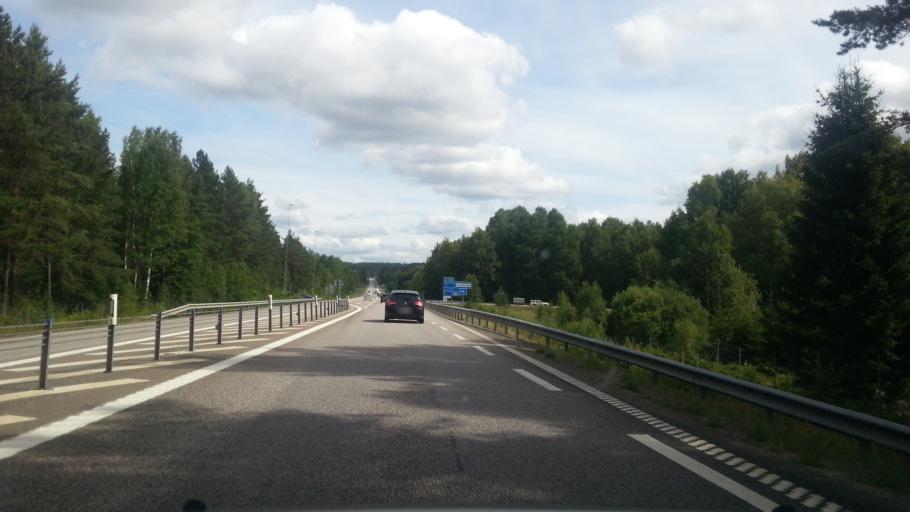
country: SE
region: Vaestra Goetaland
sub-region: Gullspangs Kommun
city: Anderstorp
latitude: 58.9265
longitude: 14.4145
